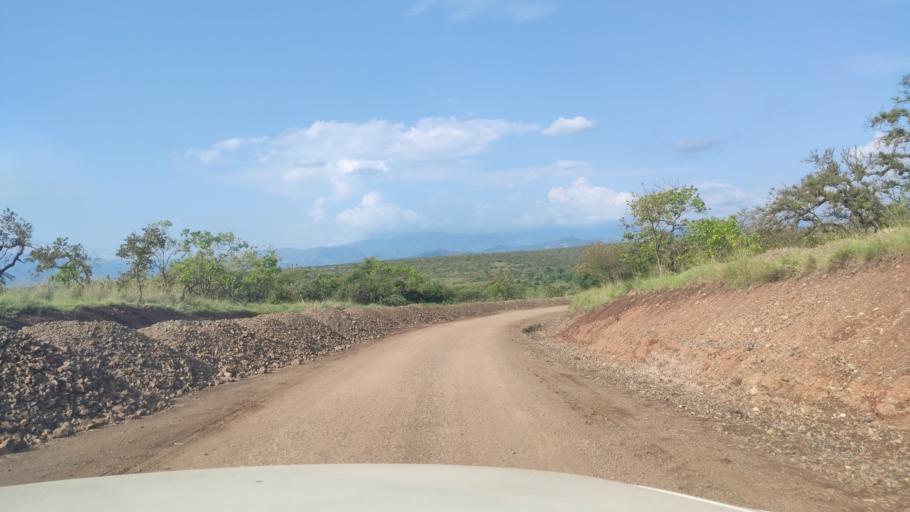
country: ET
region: Southern Nations, Nationalities, and People's Region
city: Felege Neway
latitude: 6.4325
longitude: 37.2649
